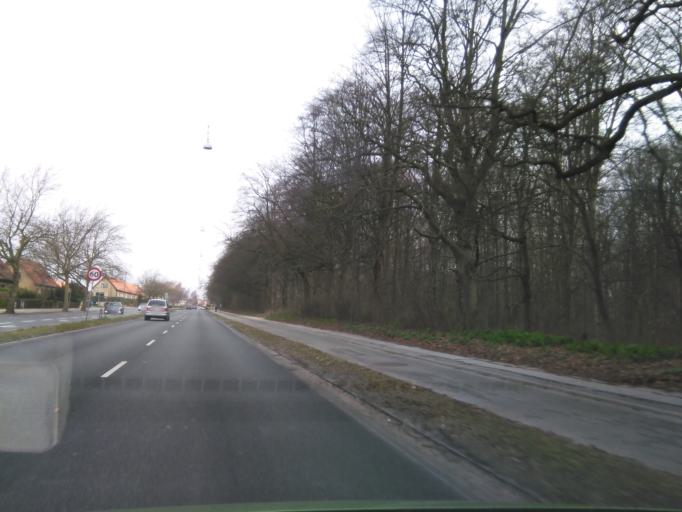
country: DK
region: Central Jutland
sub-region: Arhus Kommune
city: Arhus
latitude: 56.1795
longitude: 10.2184
